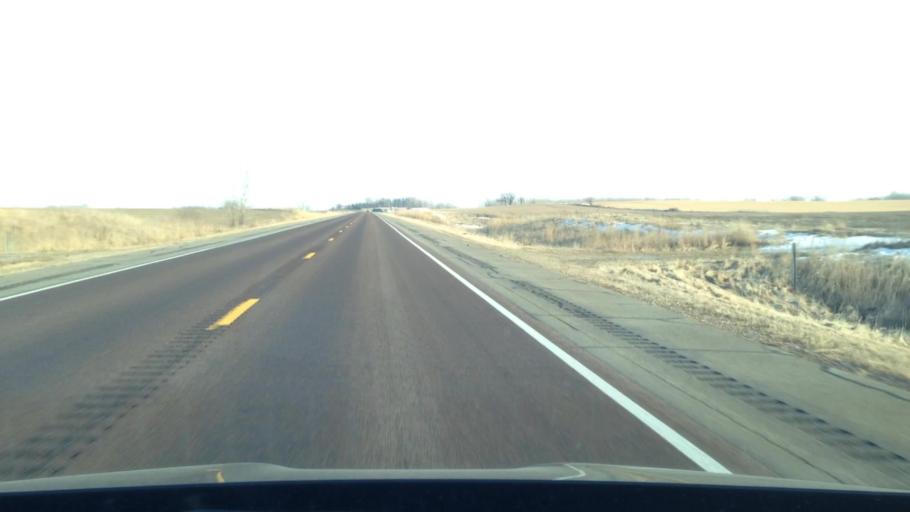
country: US
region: Minnesota
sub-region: Goodhue County
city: Goodhue
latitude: 44.4308
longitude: -92.6186
